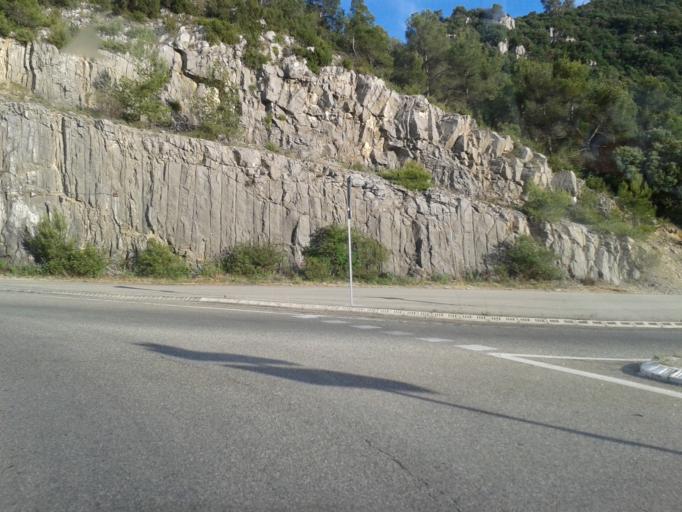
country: FR
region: Provence-Alpes-Cote d'Azur
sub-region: Departement du Vaucluse
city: Beaumont-de-Pertuis
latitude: 43.6887
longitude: 5.6669
